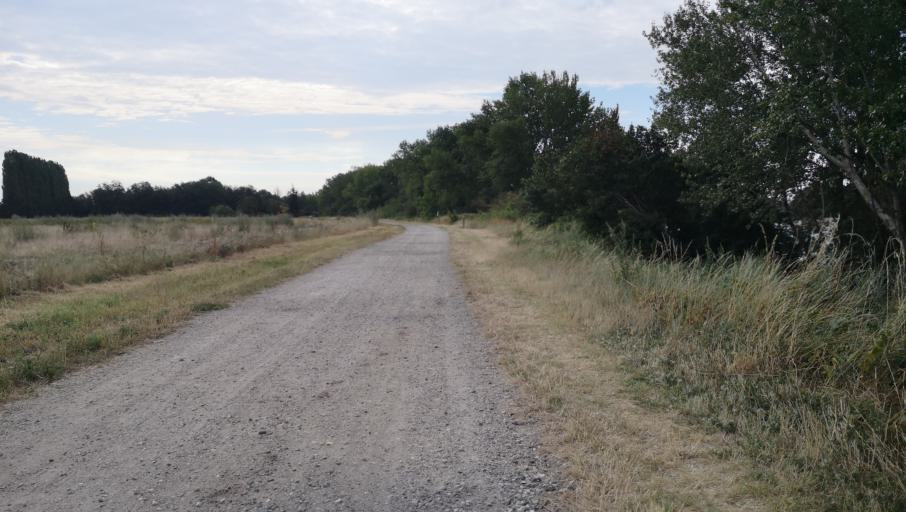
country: FR
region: Centre
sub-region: Departement du Loiret
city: Checy
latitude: 47.8873
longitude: 2.0200
